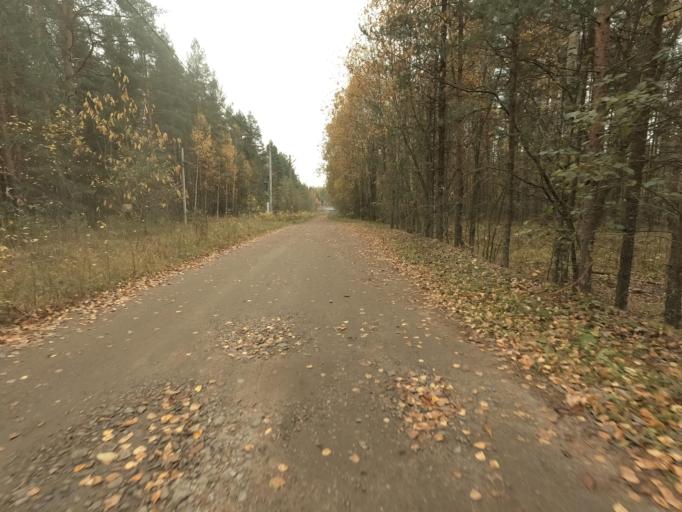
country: RU
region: Leningrad
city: Kirovsk
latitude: 59.8552
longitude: 30.9904
